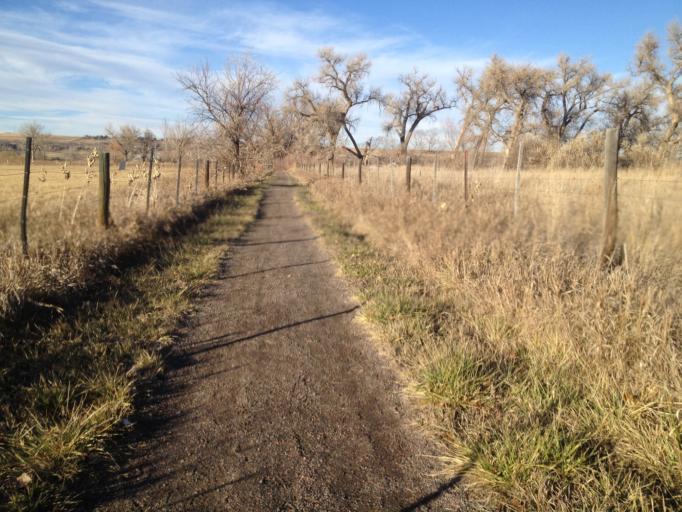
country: US
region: Colorado
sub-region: Boulder County
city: Gunbarrel
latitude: 40.0428
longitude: -105.1442
